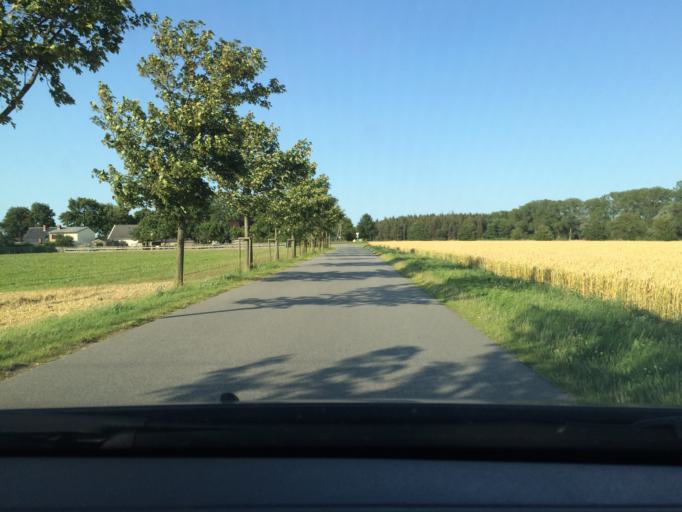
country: DE
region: Mecklenburg-Vorpommern
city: Niepars
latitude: 54.3479
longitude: 12.9223
